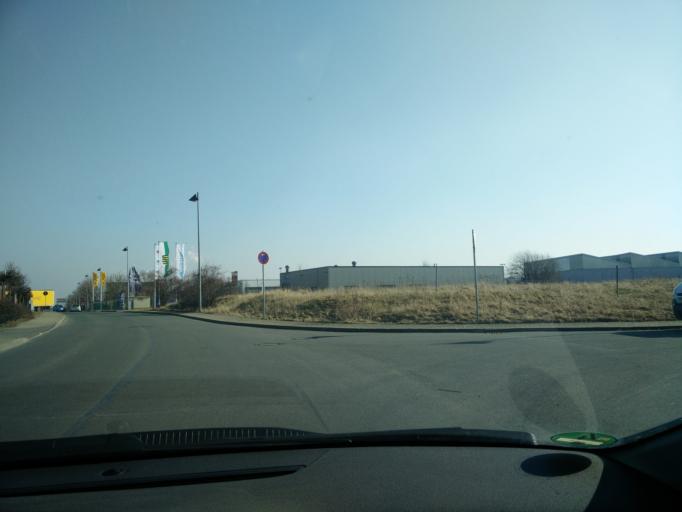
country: DE
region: Saxony
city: Wittgensdorf
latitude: 50.8675
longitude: 12.8498
